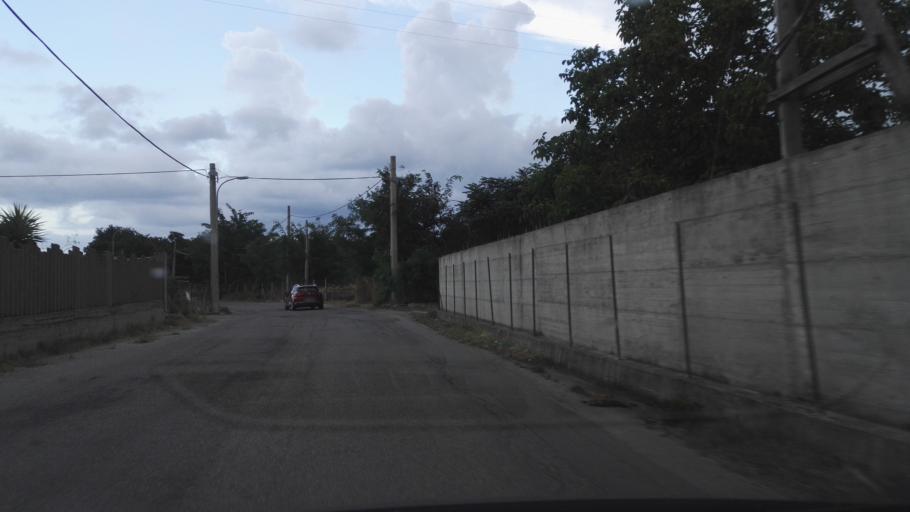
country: IT
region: Calabria
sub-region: Provincia di Reggio Calabria
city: Caulonia Marina
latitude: 38.3514
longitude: 16.4733
